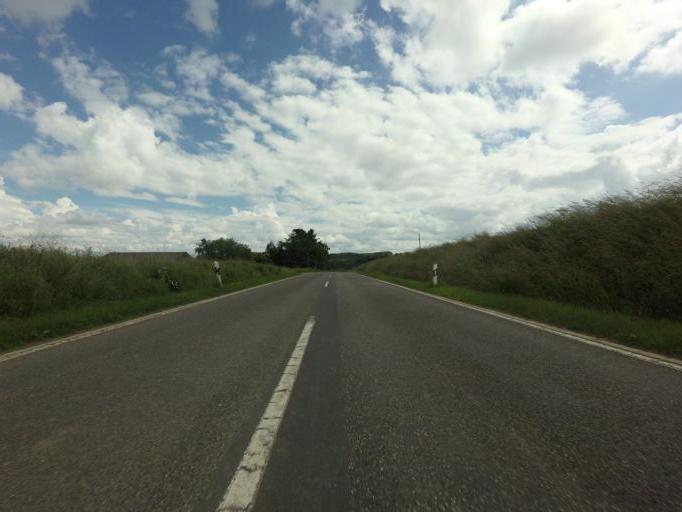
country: DE
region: Rheinland-Pfalz
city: Monreal
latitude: 50.2846
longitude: 7.1533
